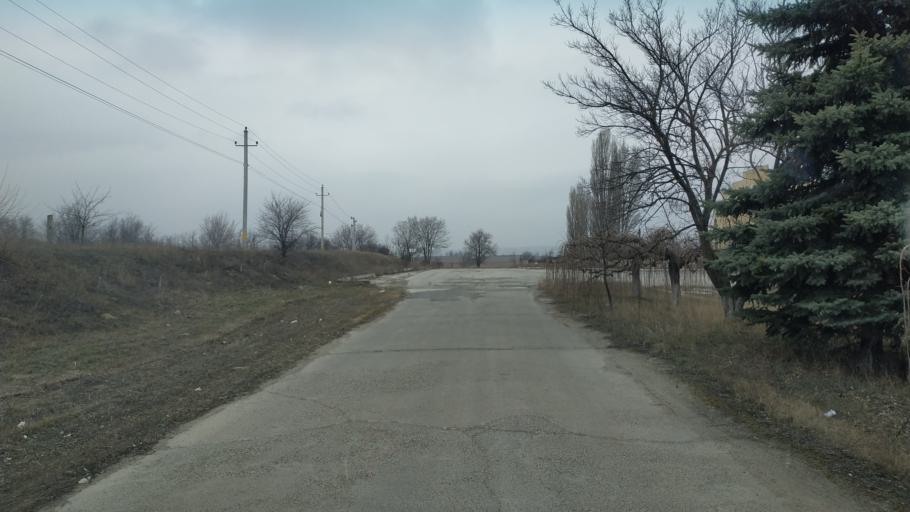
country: MD
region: Chisinau
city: Singera
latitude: 46.9126
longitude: 29.0055
